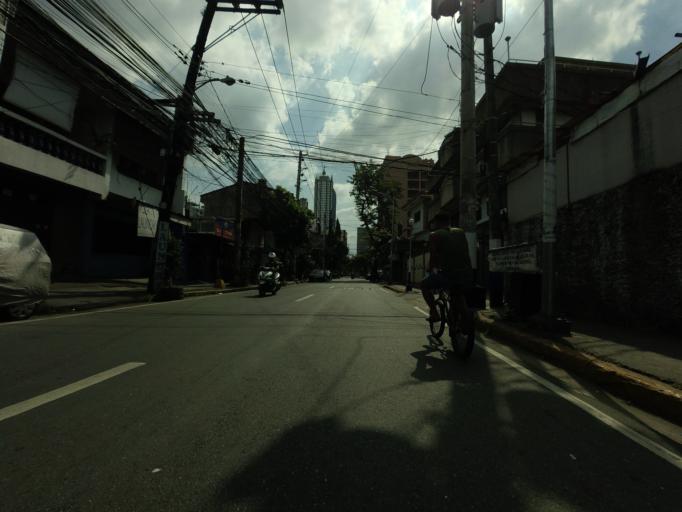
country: PH
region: Metro Manila
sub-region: City of Manila
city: Port Area
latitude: 14.5666
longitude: 120.9966
